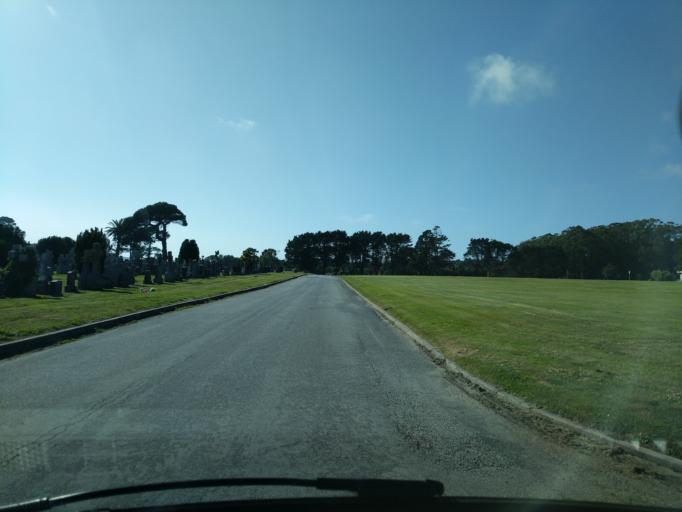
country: US
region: California
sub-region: San Mateo County
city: Colma
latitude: 37.6724
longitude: -122.4441
